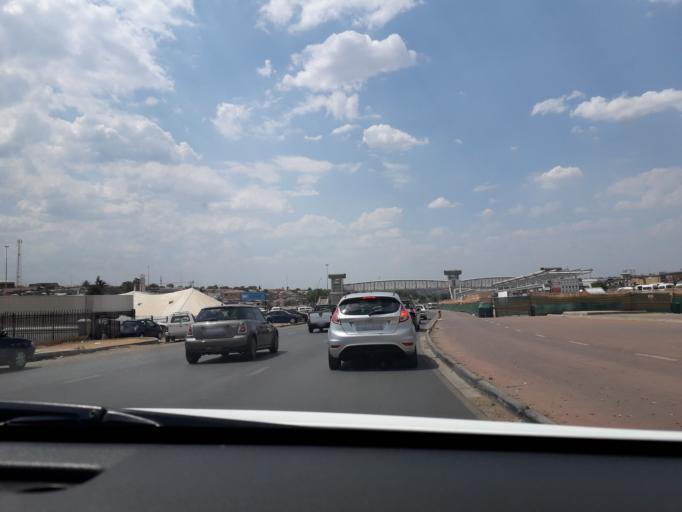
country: ZA
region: Gauteng
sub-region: Ekurhuleni Metropolitan Municipality
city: Tembisa
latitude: -26.0293
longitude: 28.1936
